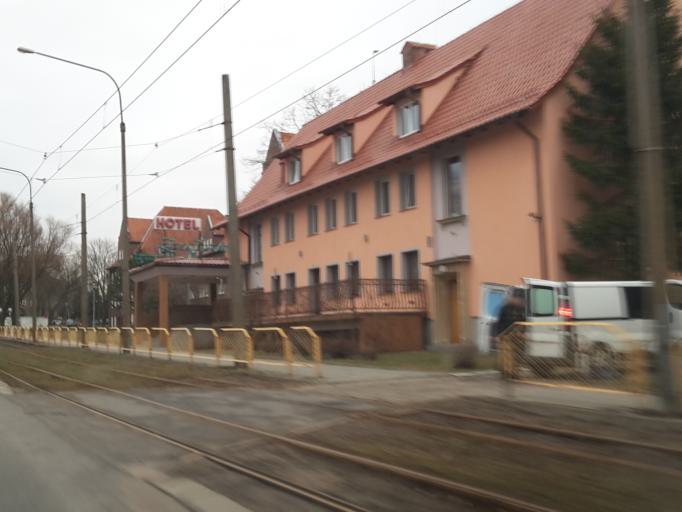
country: PL
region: Warmian-Masurian Voivodeship
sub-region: Powiat elblaski
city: Elblag
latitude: 54.1711
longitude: 19.4124
